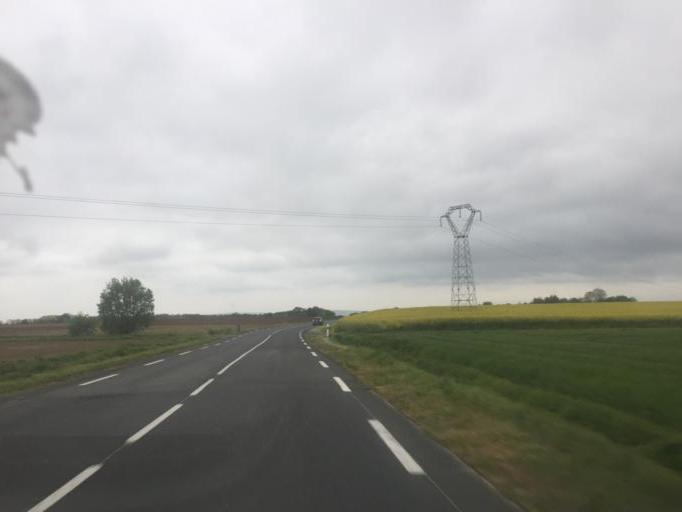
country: FR
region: Rhone-Alpes
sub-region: Departement de l'Ain
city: Reyrieux
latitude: 45.9377
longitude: 4.8435
